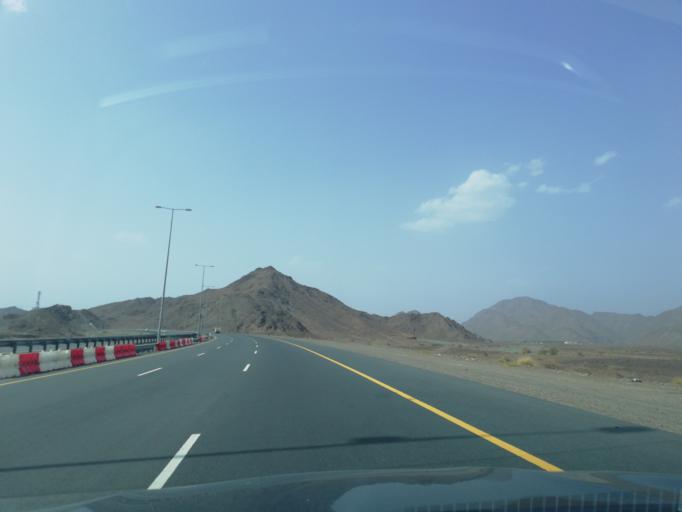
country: OM
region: Ash Sharqiyah
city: Ibra'
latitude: 22.9595
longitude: 58.2457
